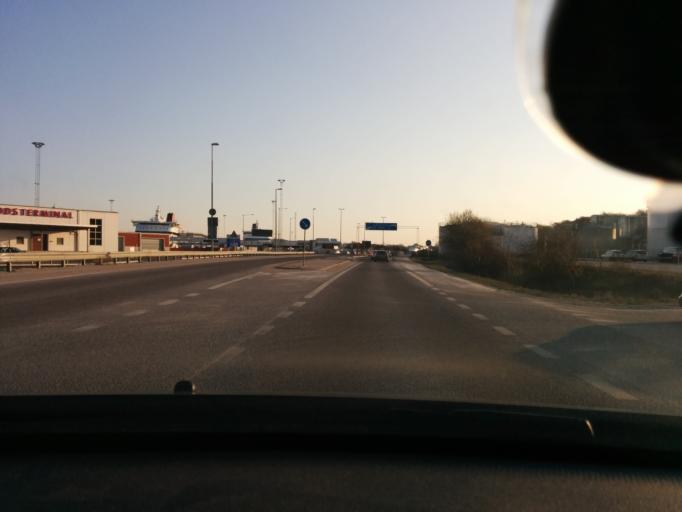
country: SE
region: Gotland
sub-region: Gotland
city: Visby
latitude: 57.6299
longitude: 18.2761
